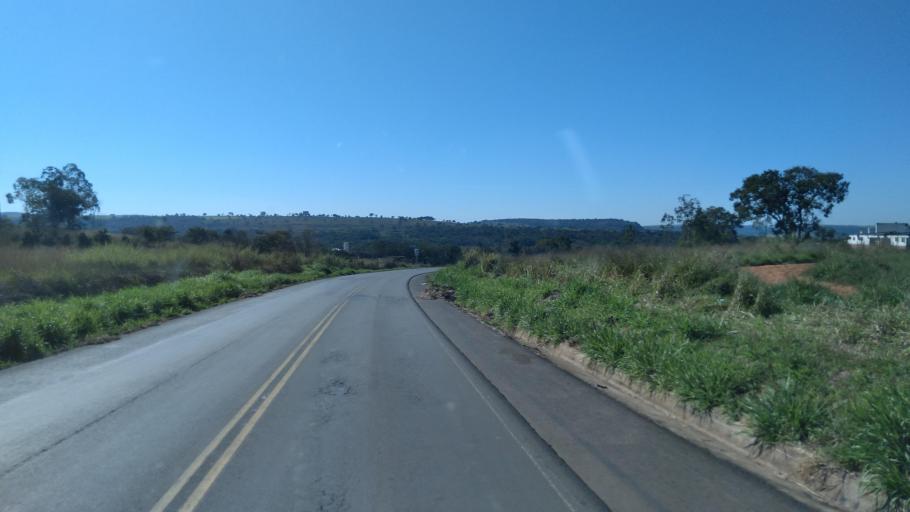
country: BR
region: Goias
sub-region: Mineiros
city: Mineiros
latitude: -17.5789
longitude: -52.5121
